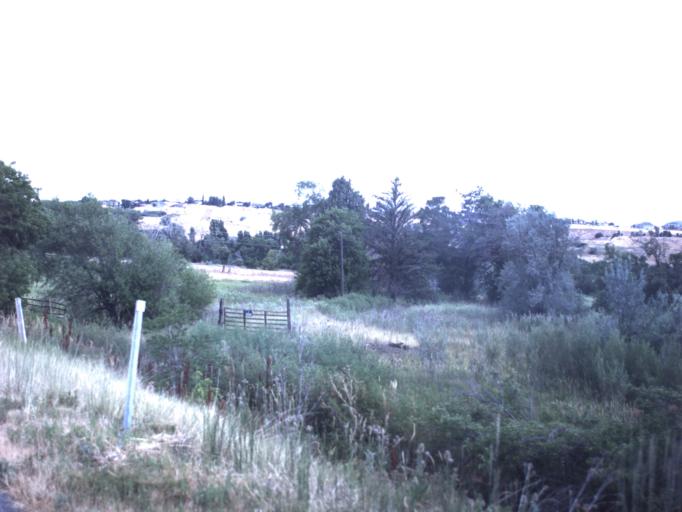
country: US
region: Utah
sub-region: Weber County
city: Washington Terrace
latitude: 41.1486
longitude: -111.9814
